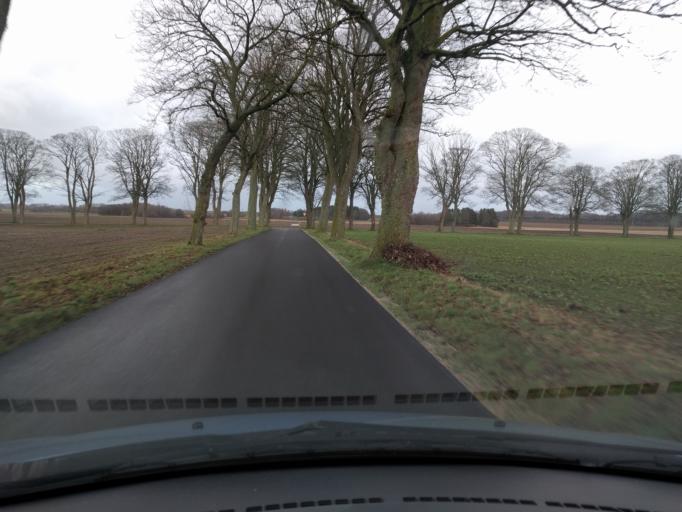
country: DK
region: South Denmark
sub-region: Kerteminde Kommune
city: Langeskov
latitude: 55.3524
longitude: 10.5431
